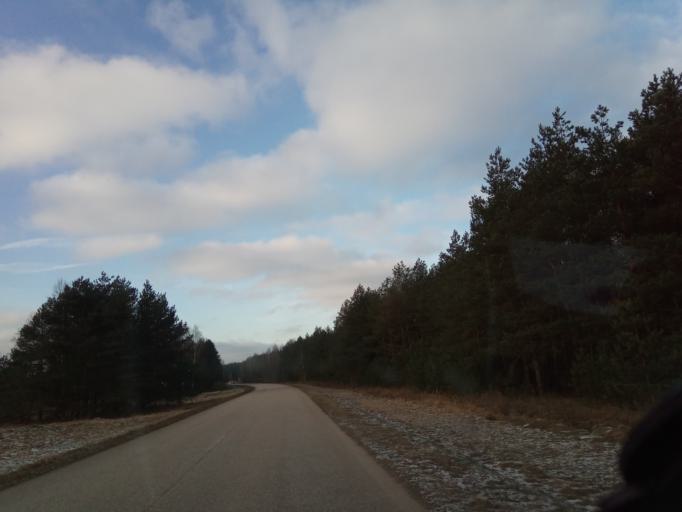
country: LT
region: Alytaus apskritis
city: Druskininkai
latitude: 53.9795
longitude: 24.2450
